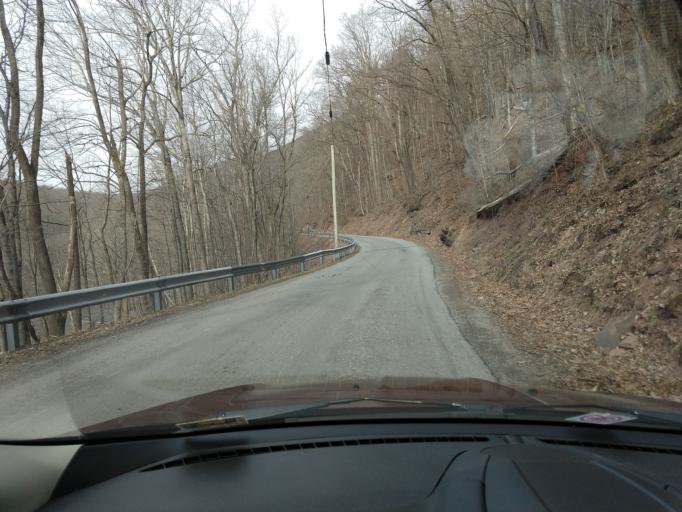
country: US
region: West Virginia
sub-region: Tucker County
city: Parsons
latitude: 39.0416
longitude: -79.6029
